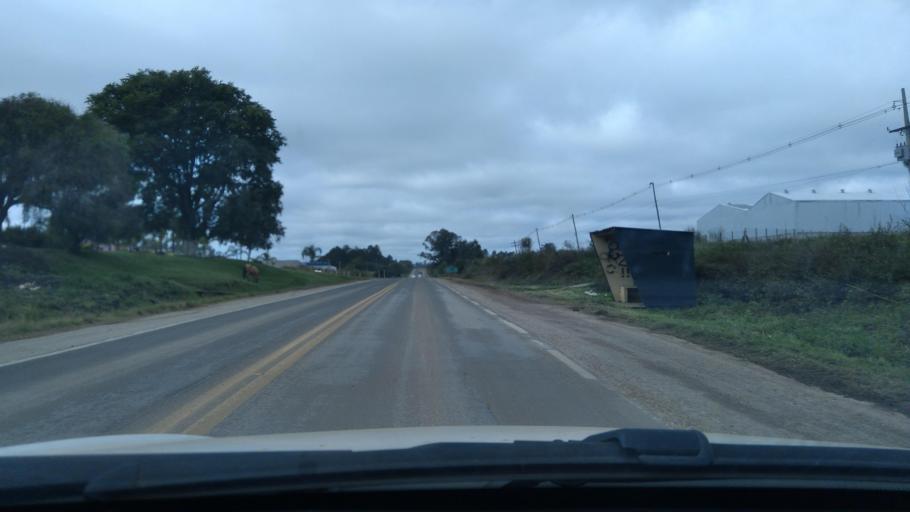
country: BR
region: Rio Grande do Sul
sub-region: Dom Pedrito
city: Dom Pedrito
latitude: -30.9682
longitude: -54.6619
